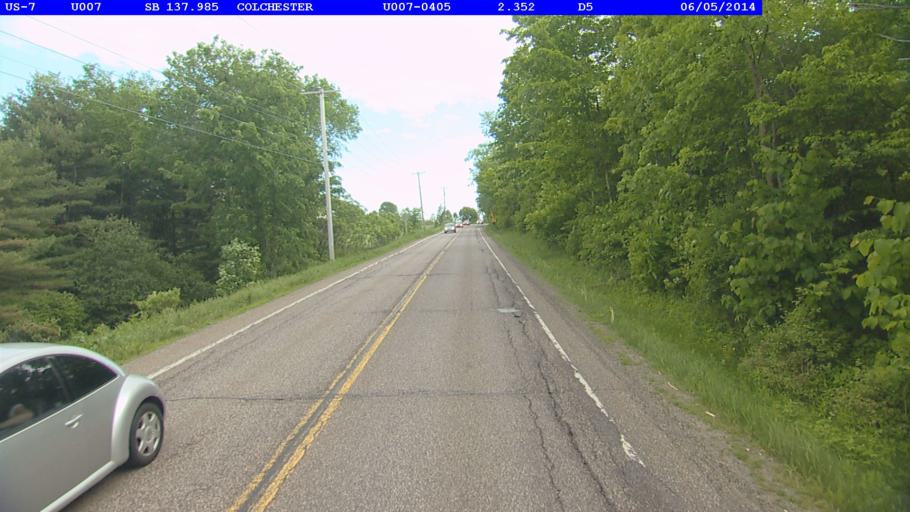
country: US
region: Vermont
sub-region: Chittenden County
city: Colchester
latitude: 44.5338
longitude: -73.1705
